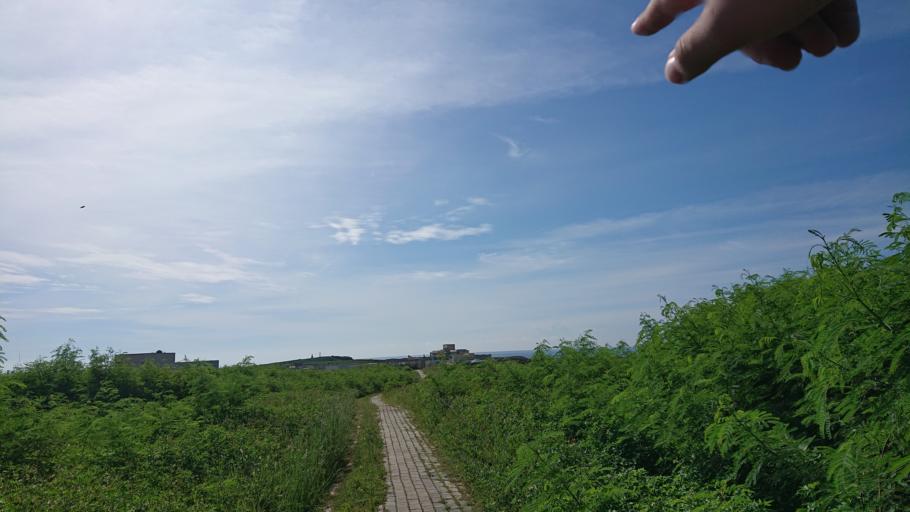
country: TW
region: Taiwan
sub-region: Penghu
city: Ma-kung
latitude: 23.6512
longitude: 119.5211
